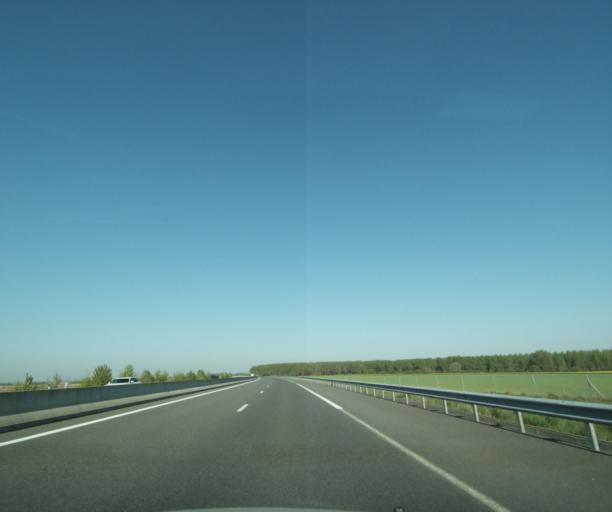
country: FR
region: Centre
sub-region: Departement du Loiret
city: Corbeilles
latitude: 48.0945
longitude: 2.5781
